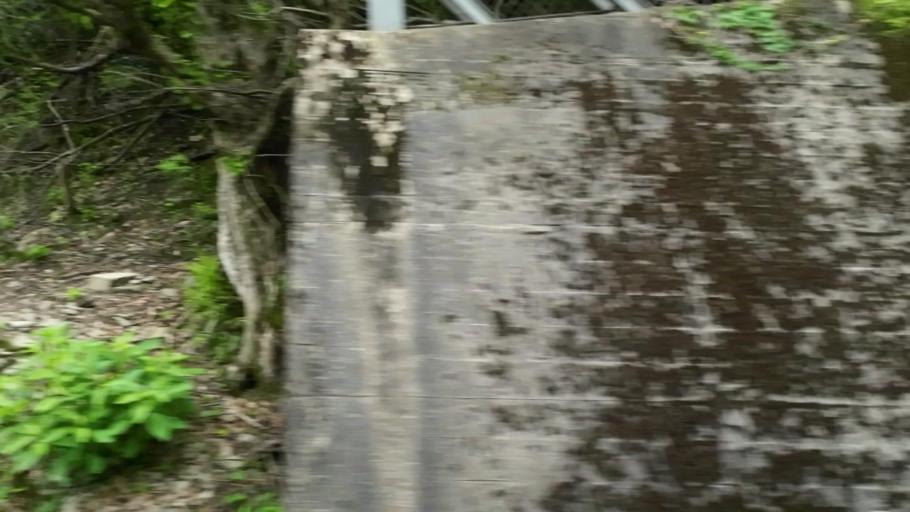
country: JP
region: Tokushima
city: Ikedacho
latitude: 33.9089
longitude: 133.7575
